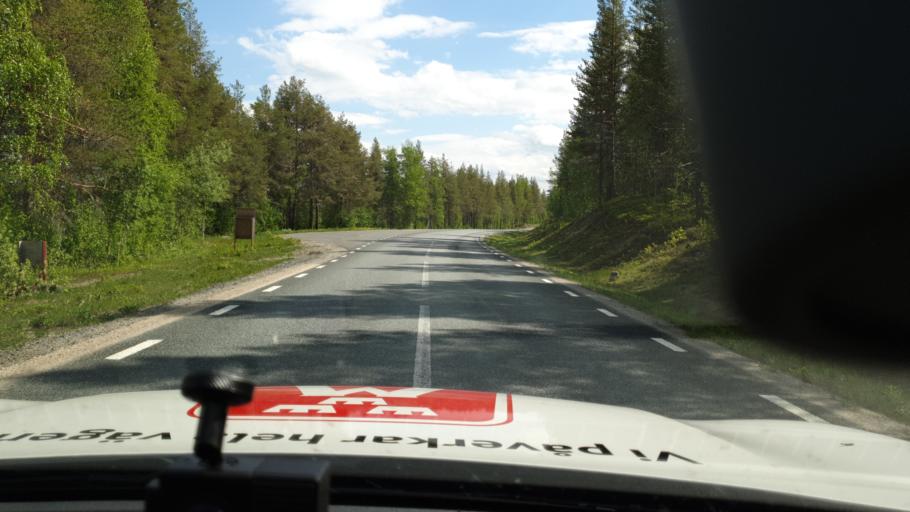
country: SE
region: Vaesterbotten
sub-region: Sorsele Kommun
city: Sorsele
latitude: 65.4858
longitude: 17.5583
